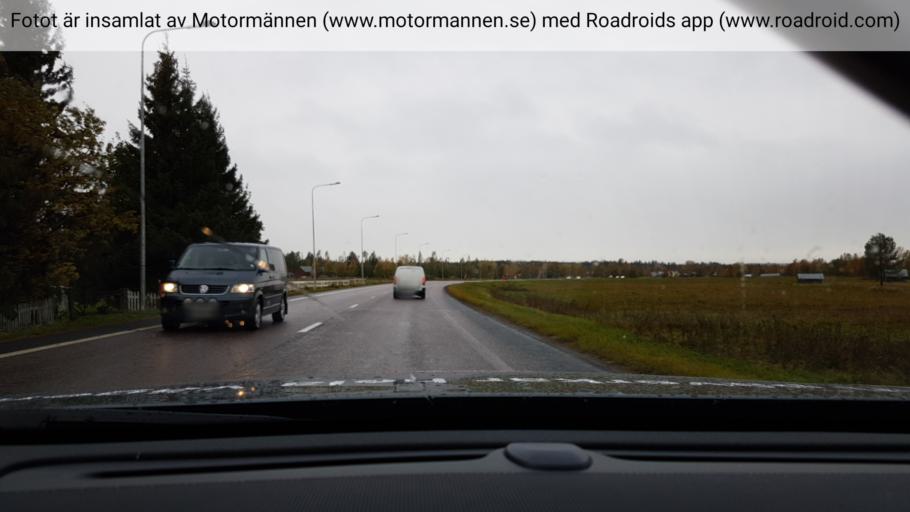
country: SE
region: Norrbotten
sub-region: Lulea Kommun
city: Bergnaset
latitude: 65.5816
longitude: 22.0489
